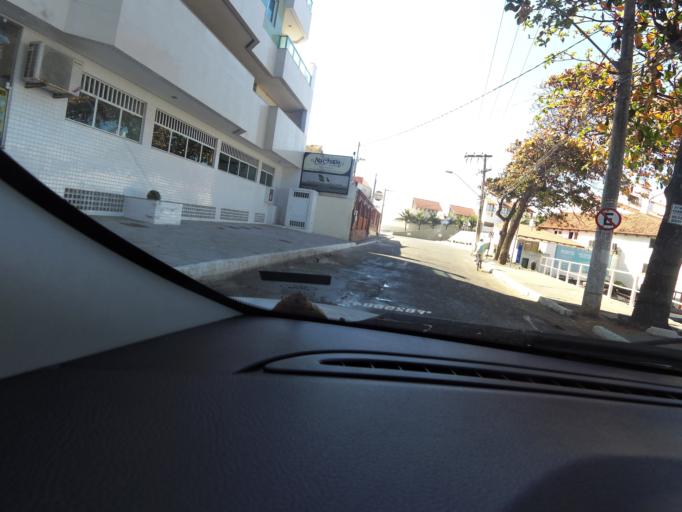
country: BR
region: Espirito Santo
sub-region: Guarapari
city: Guarapari
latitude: -20.6623
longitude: -40.4963
